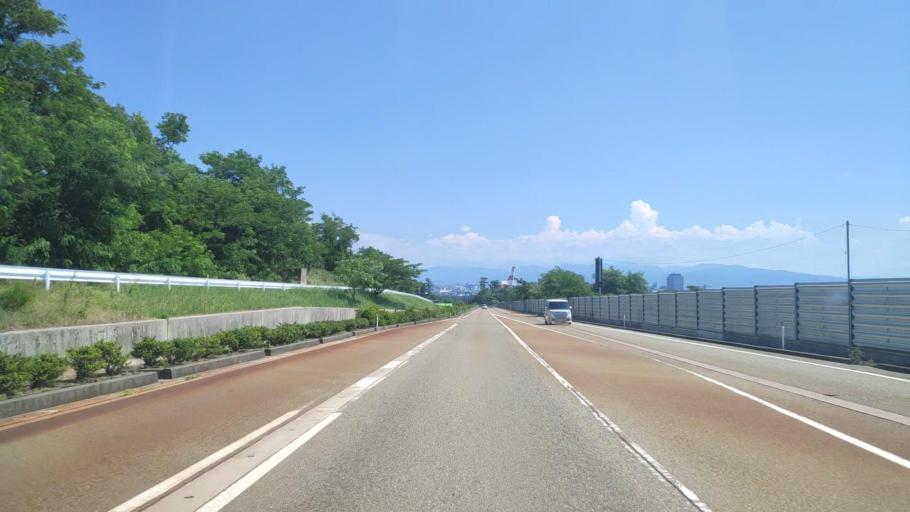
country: JP
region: Ishikawa
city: Kanazawa-shi
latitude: 36.6230
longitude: 136.6169
